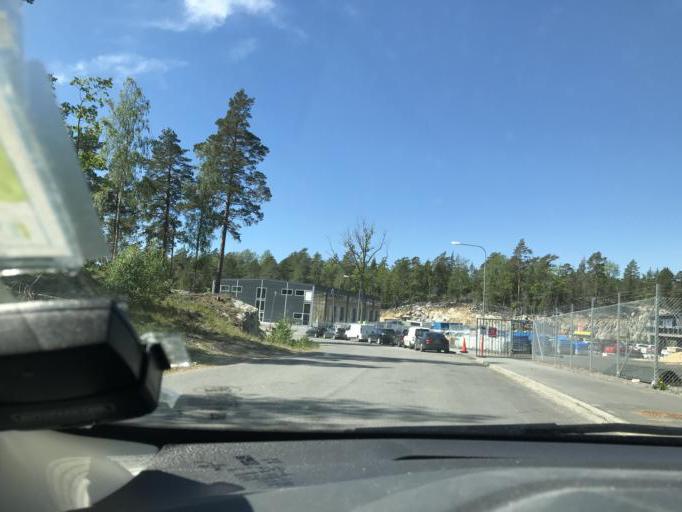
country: SE
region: Stockholm
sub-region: Botkyrka Kommun
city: Alby
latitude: 59.2146
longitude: 17.8469
